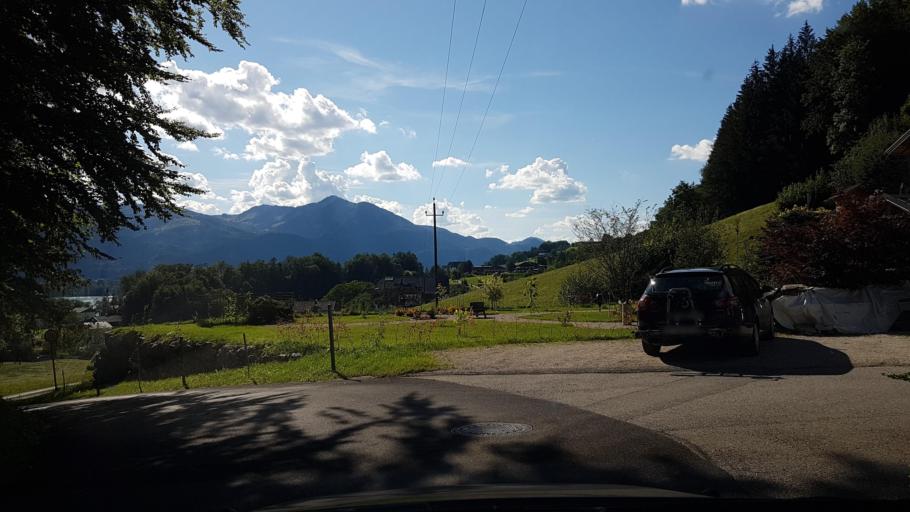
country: AT
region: Upper Austria
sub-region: Politischer Bezirk Gmunden
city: Sankt Wolfgang im Salzkammergut
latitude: 47.7355
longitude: 13.4668
